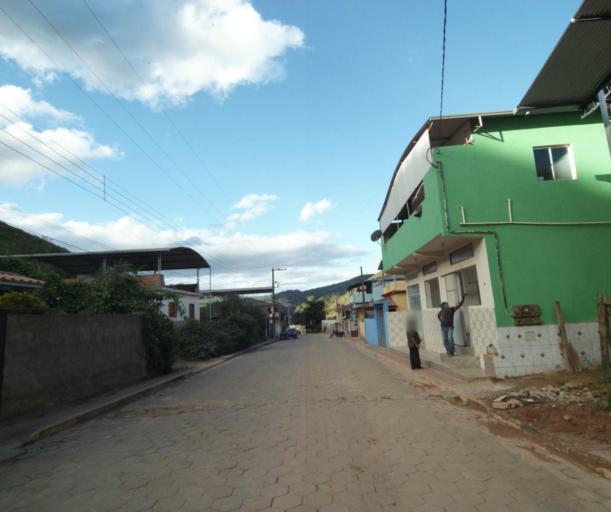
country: BR
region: Espirito Santo
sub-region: Guacui
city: Guacui
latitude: -20.6243
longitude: -41.6878
